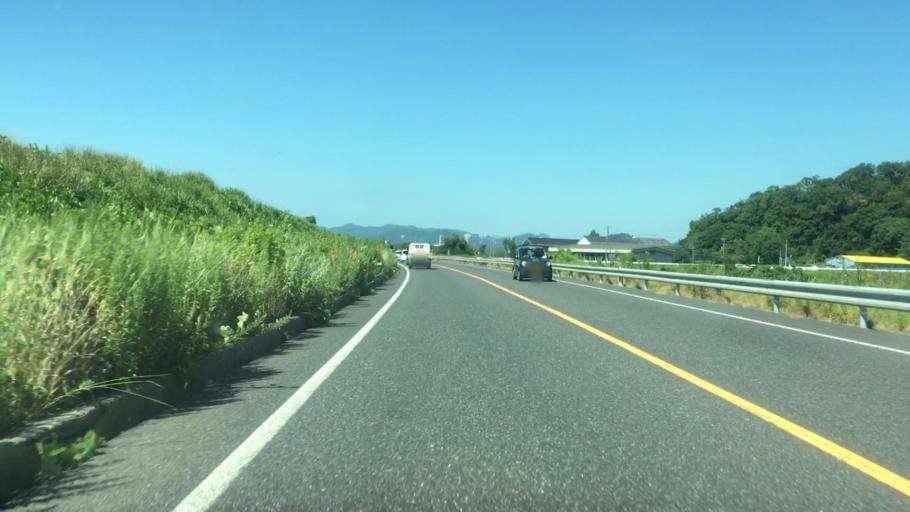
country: JP
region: Tottori
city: Tottori
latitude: 35.4479
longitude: 134.2129
